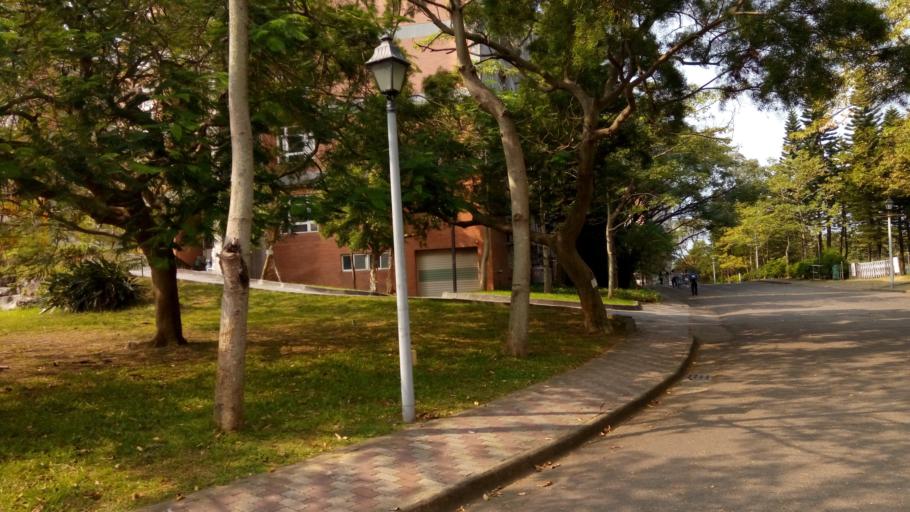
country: TW
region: Taiwan
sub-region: Hsinchu
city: Hsinchu
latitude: 24.7596
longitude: 120.9529
